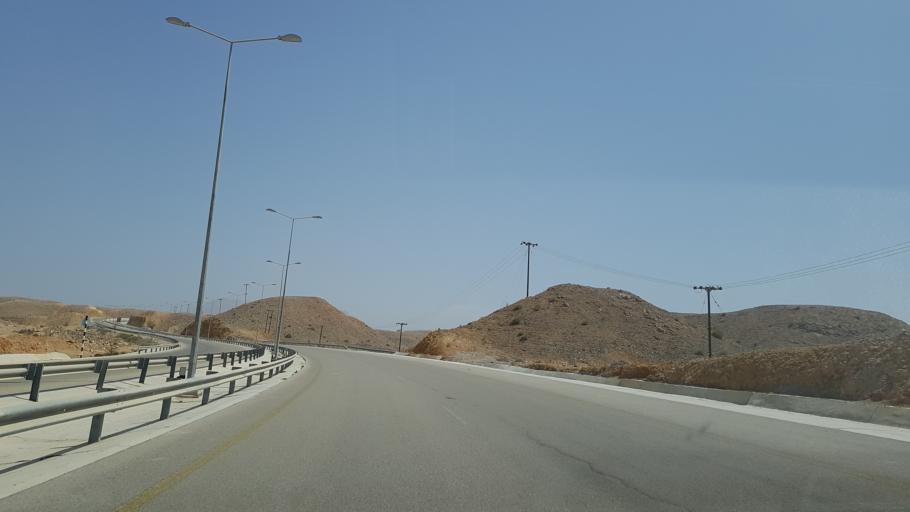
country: OM
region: Muhafazat Masqat
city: Muscat
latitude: 23.1316
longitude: 58.9723
